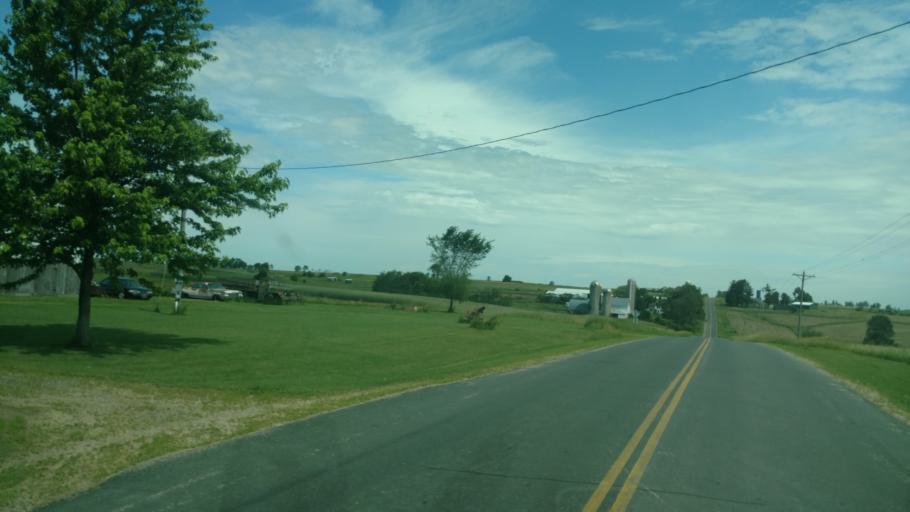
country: US
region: Wisconsin
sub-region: Vernon County
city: Hillsboro
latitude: 43.7412
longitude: -90.4329
